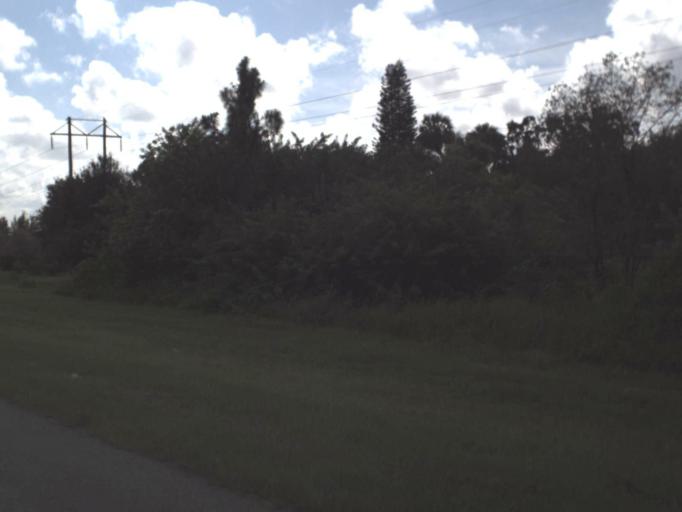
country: US
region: Florida
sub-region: Collier County
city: Immokalee
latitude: 26.3924
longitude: -81.3797
